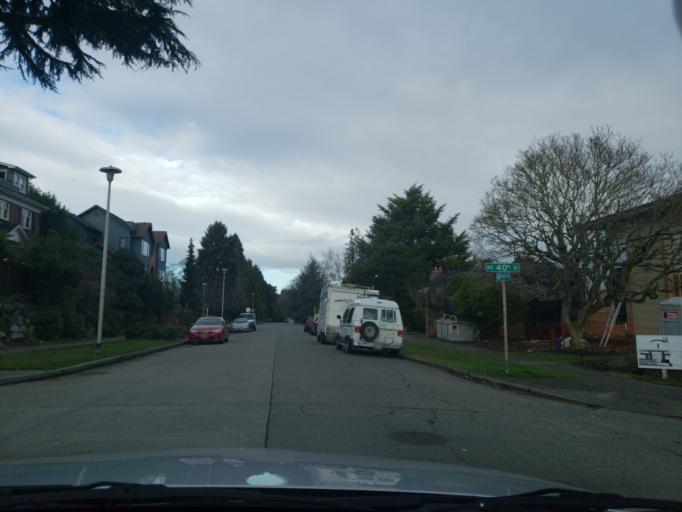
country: US
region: Washington
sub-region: King County
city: Yarrow Point
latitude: 47.6576
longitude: -122.2767
